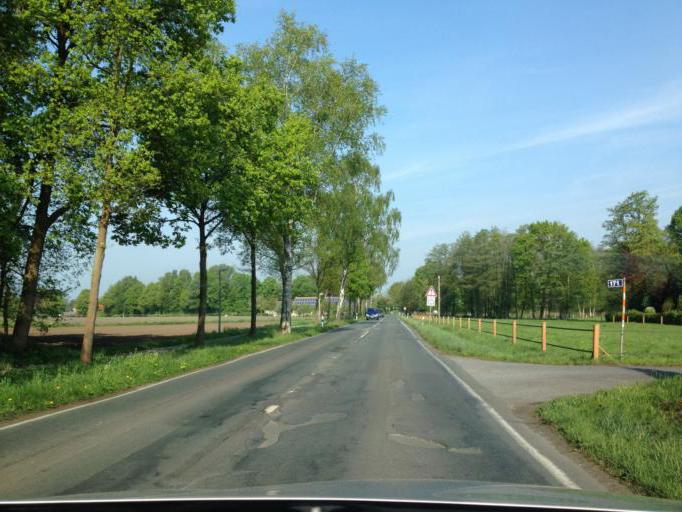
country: DE
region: North Rhine-Westphalia
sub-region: Regierungsbezirk Detmold
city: Guetersloh
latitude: 51.8987
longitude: 8.4443
